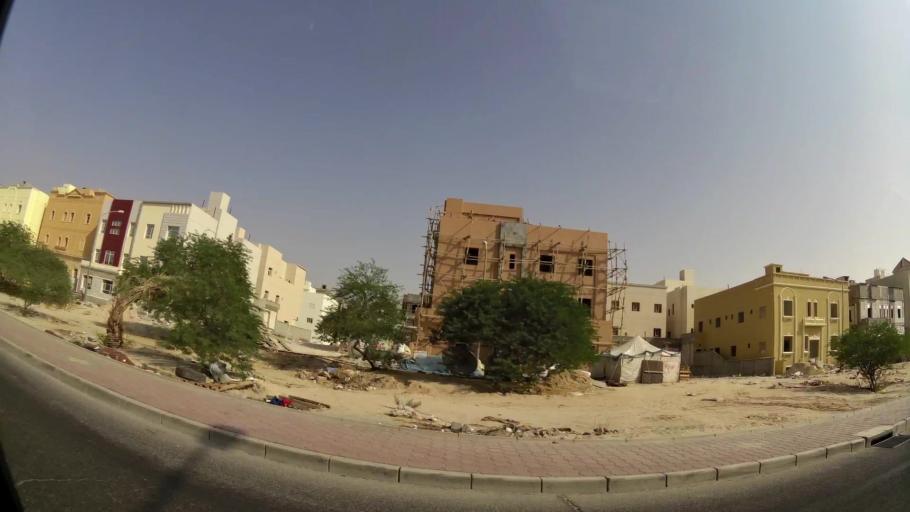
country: KW
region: Muhafazat al Jahra'
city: Al Jahra'
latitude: 29.3175
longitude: 47.6780
